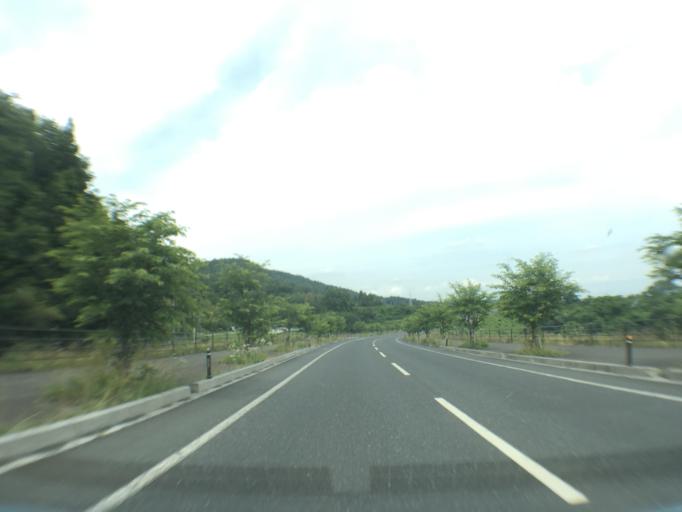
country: JP
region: Iwate
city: Ichinoseki
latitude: 38.9405
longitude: 141.0751
